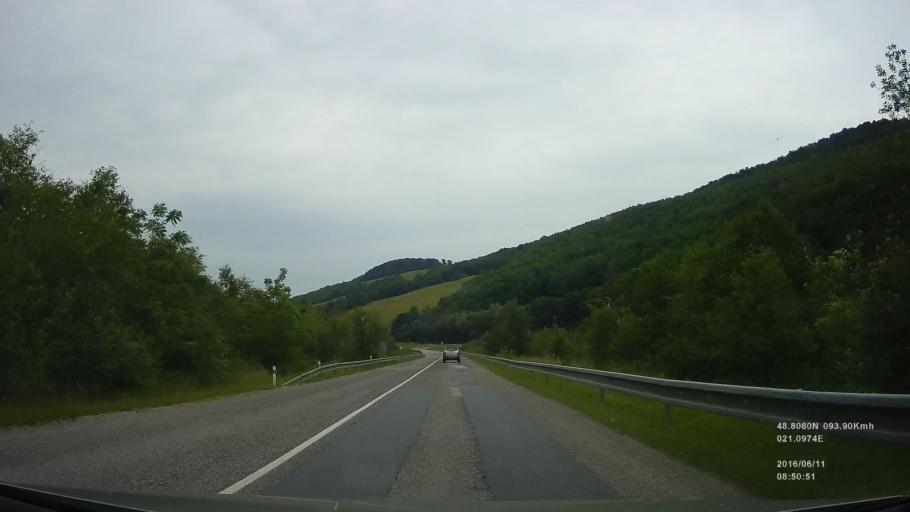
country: SK
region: Kosicky
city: Kosice
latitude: 48.8017
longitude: 21.1051
